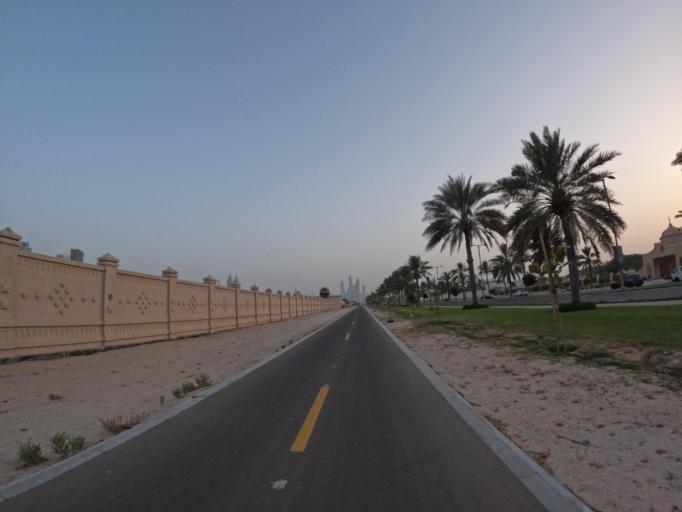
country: AE
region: Dubai
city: Dubai
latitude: 25.1191
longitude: 55.1758
